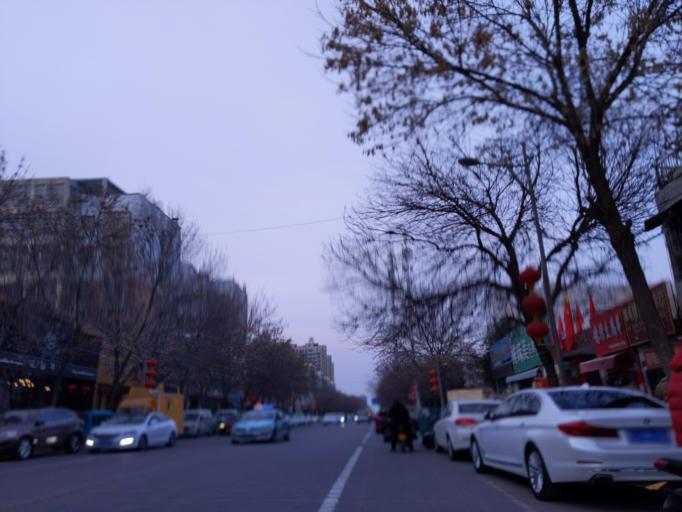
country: CN
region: Henan Sheng
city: Zhongyuanlu
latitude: 35.7831
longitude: 115.0391
